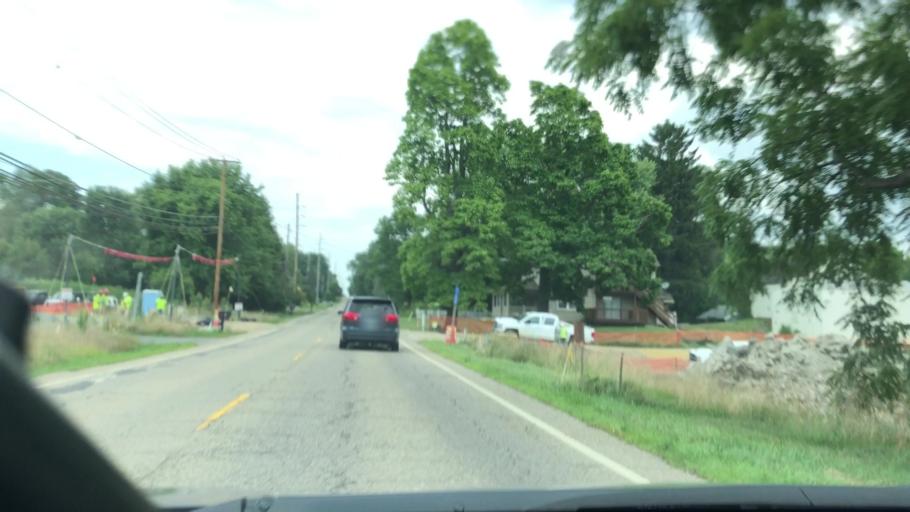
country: US
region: Ohio
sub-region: Summit County
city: New Franklin
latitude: 40.9234
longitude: -81.5356
